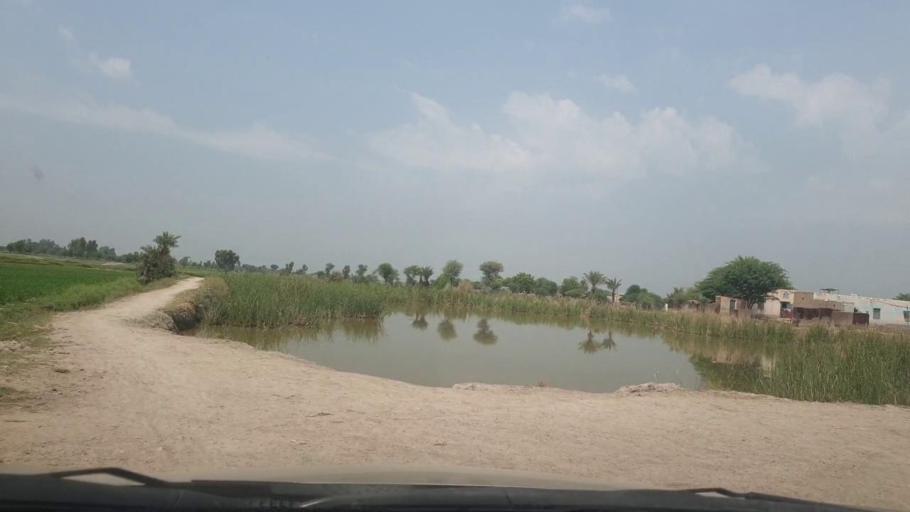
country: PK
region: Sindh
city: Ratodero
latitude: 27.6947
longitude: 68.2511
